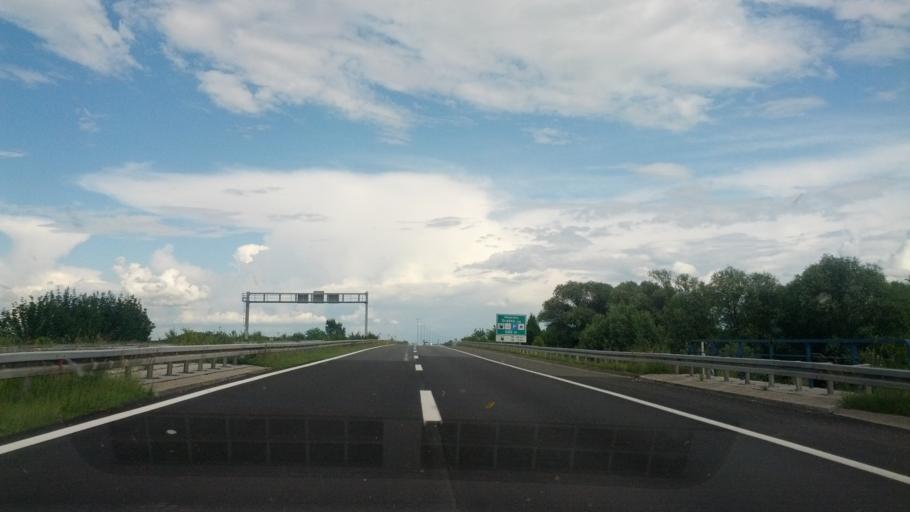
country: HR
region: Zagrebacka
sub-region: Grad Samobor
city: Samobor
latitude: 45.8294
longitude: 15.7297
